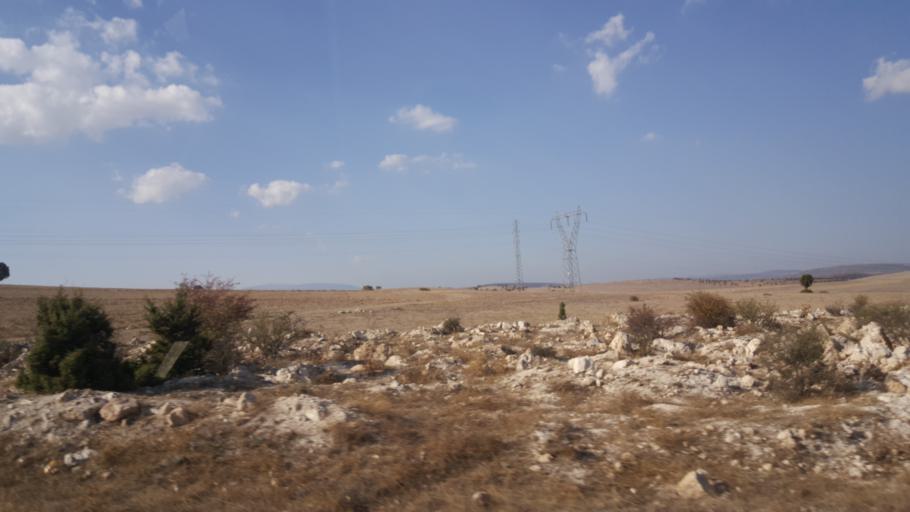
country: TR
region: Eskisehir
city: Kirka
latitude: 39.3197
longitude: 30.5538
